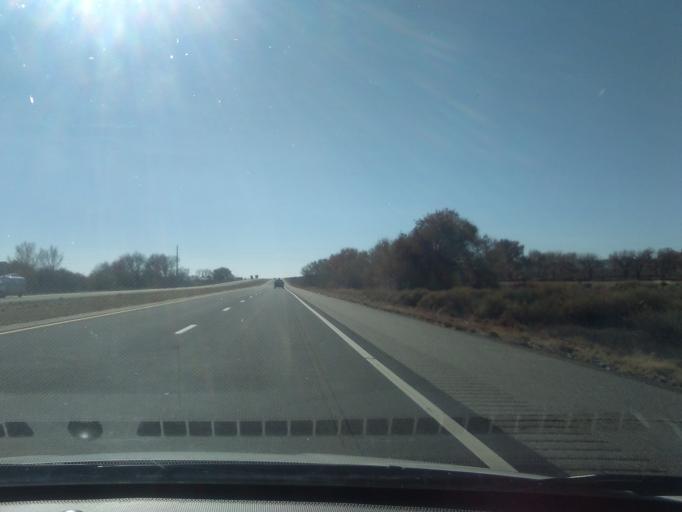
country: US
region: New Mexico
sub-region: Valencia County
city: Jarales
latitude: 34.6197
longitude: -106.7844
